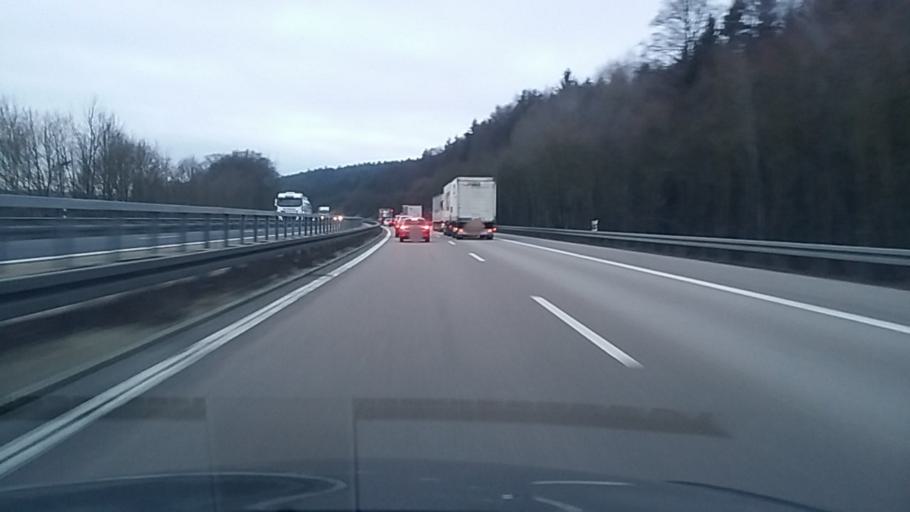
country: DE
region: Bavaria
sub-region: Upper Palatinate
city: Velburg
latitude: 49.2190
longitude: 11.6485
